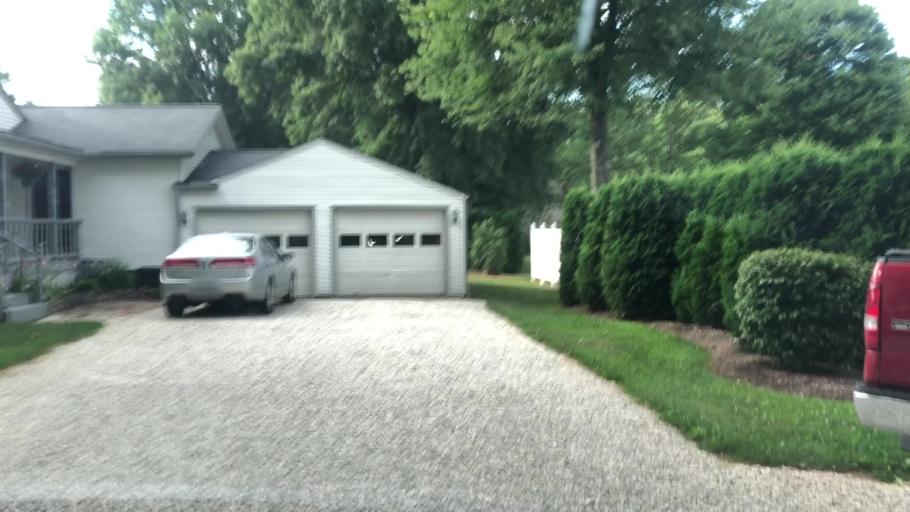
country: US
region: Ohio
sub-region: Summit County
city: Montrose-Ghent
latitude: 41.0994
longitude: -81.6890
